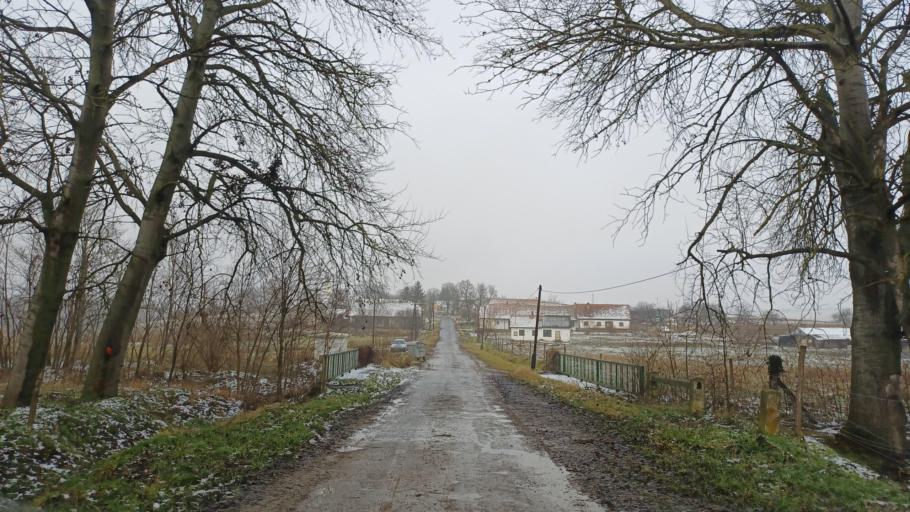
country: HU
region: Tolna
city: Gyonk
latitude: 46.5888
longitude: 18.5145
